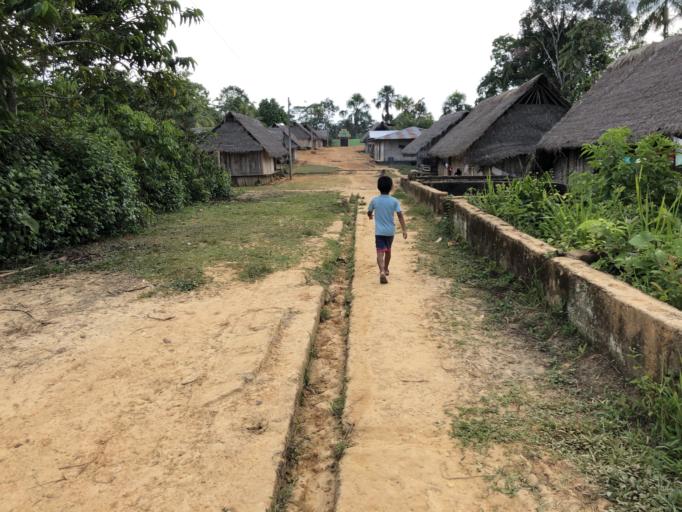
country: PE
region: Loreto
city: Puerto Galilea
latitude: -4.0537
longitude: -77.7605
